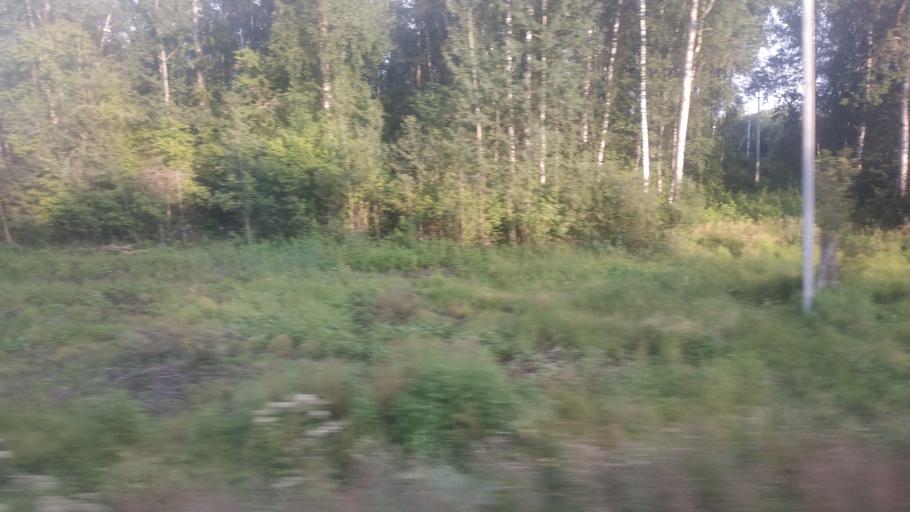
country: RU
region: Moskovskaya
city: Kerva
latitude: 55.5499
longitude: 39.6898
